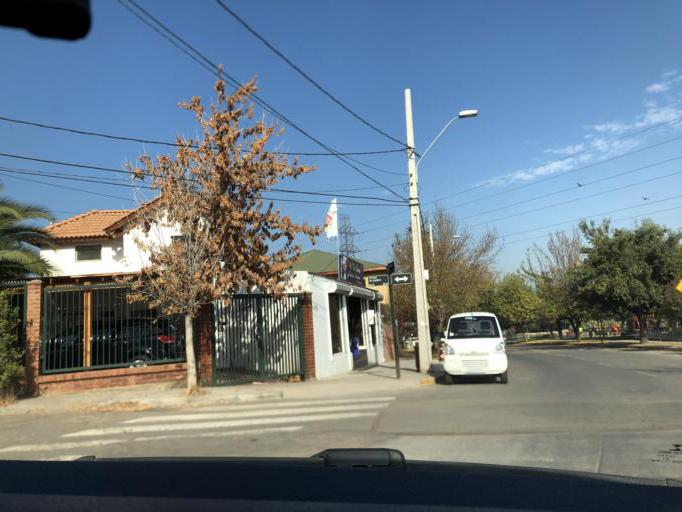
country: CL
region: Santiago Metropolitan
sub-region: Provincia de Cordillera
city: Puente Alto
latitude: -33.5894
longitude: -70.5380
